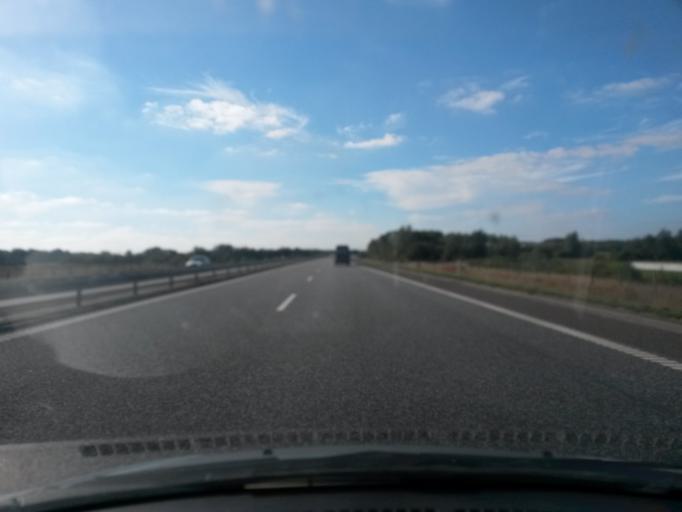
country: DK
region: Central Jutland
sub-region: Ikast-Brande Kommune
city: Ikast
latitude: 56.1181
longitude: 9.1655
